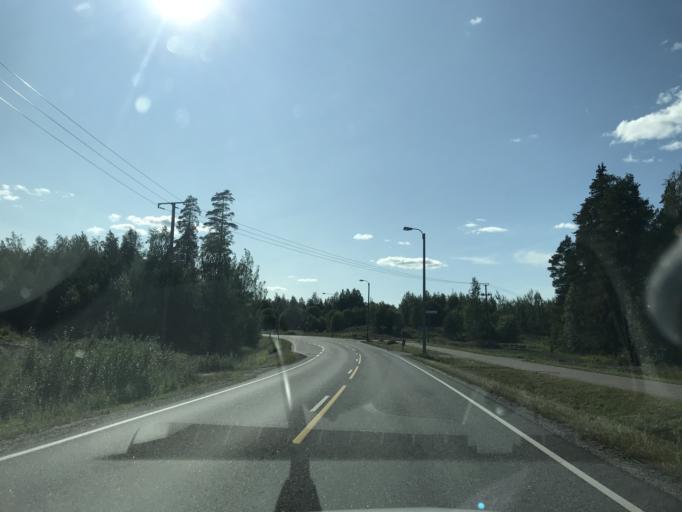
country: FI
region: Uusimaa
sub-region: Helsinki
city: Nurmijaervi
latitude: 60.3853
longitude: 24.7097
